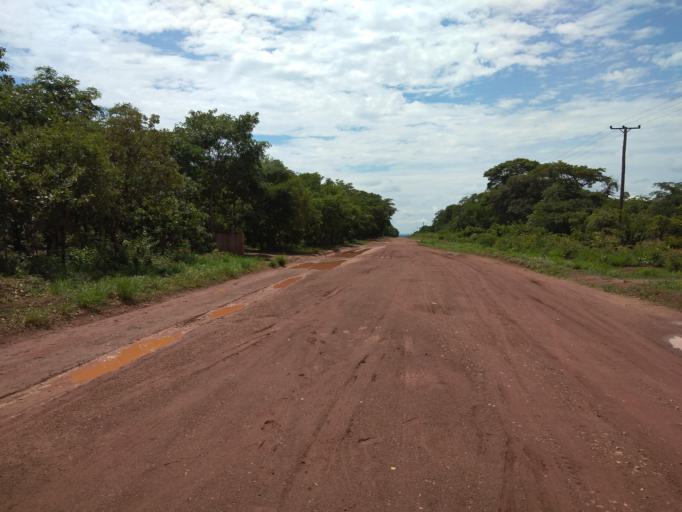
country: ZM
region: Copperbelt
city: Luanshya
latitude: -13.4836
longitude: 28.6993
